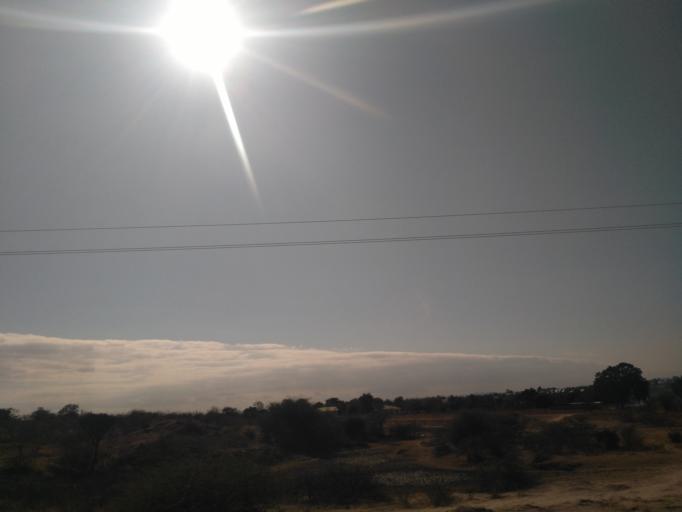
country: TZ
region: Dodoma
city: Dodoma
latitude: -6.0989
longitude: 35.7487
